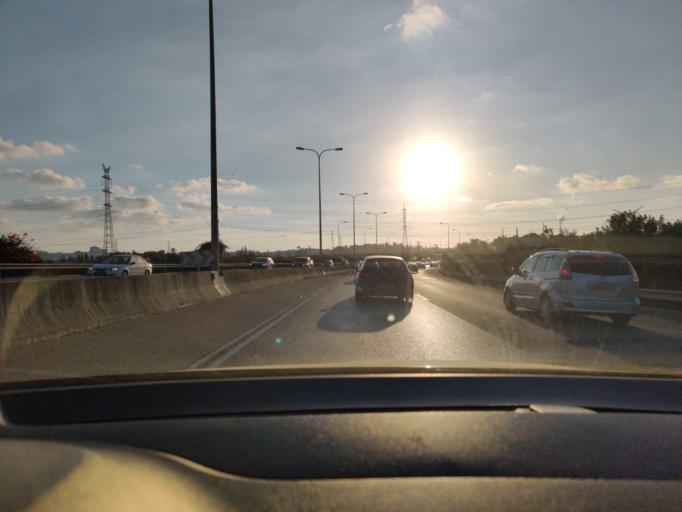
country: IL
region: Haifa
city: Hadera
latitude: 32.4461
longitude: 34.9474
